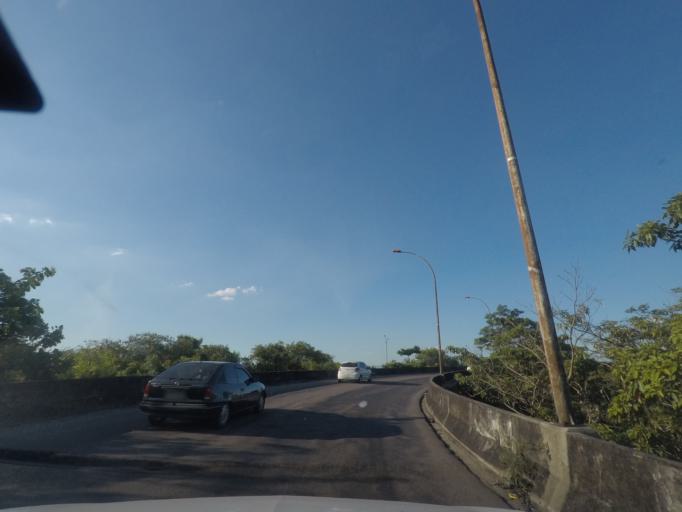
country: BR
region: Rio de Janeiro
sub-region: Duque De Caxias
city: Duque de Caxias
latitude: -22.8088
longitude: -43.2903
